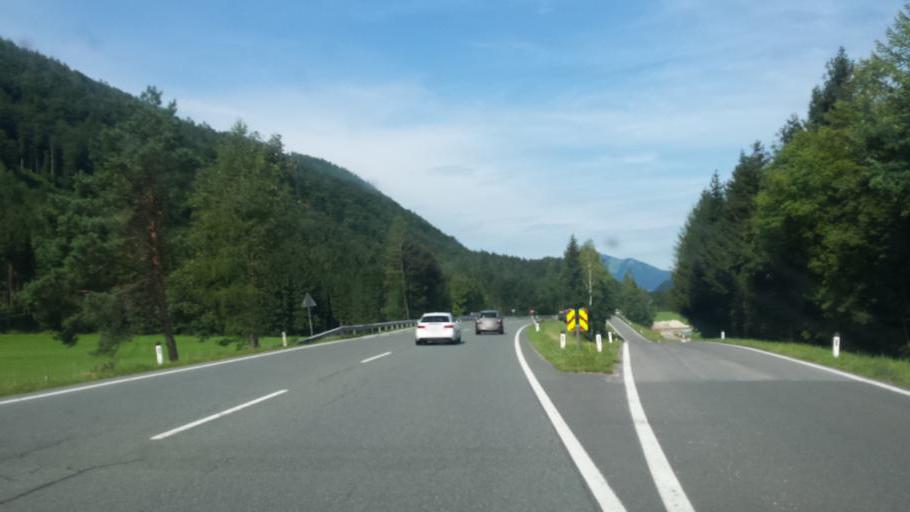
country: AT
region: Salzburg
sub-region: Politischer Bezirk Salzburg-Umgebung
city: Strobl
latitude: 47.7110
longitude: 13.5431
